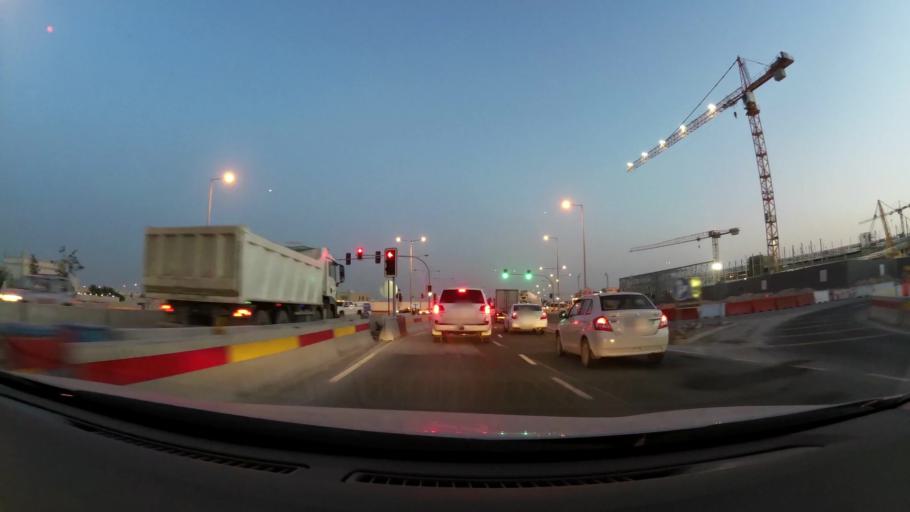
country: QA
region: Baladiyat ar Rayyan
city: Ar Rayyan
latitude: 25.3102
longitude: 51.4537
